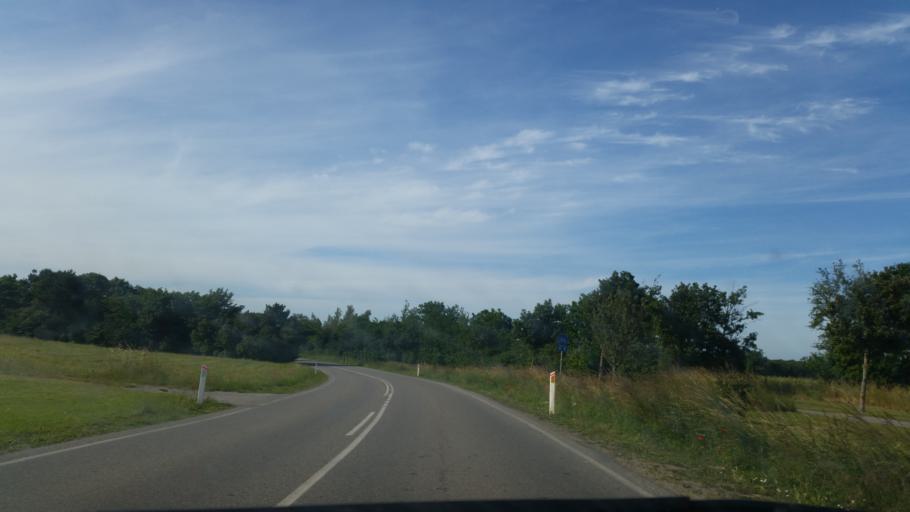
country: DK
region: Central Jutland
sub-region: Samso Kommune
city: Tranebjerg
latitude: 55.8543
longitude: 10.5731
